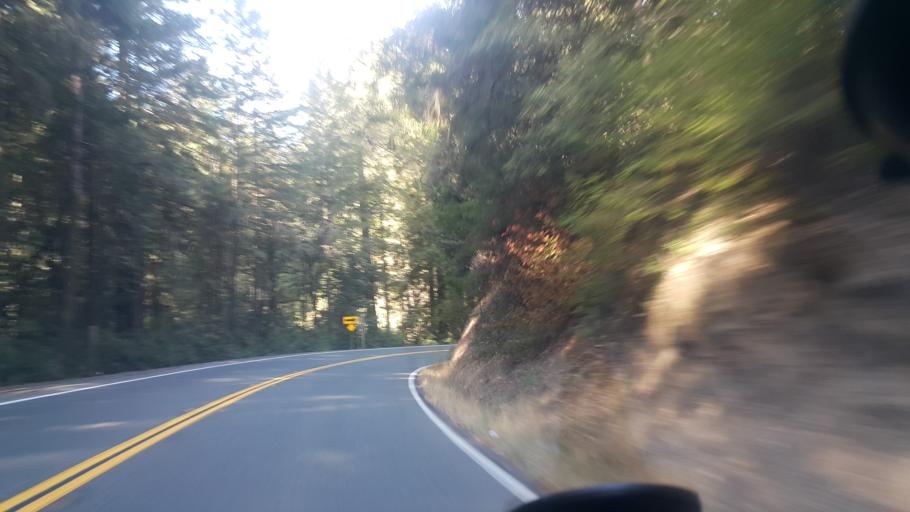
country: US
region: California
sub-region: Mendocino County
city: Brooktrails
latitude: 39.3463
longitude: -123.5215
